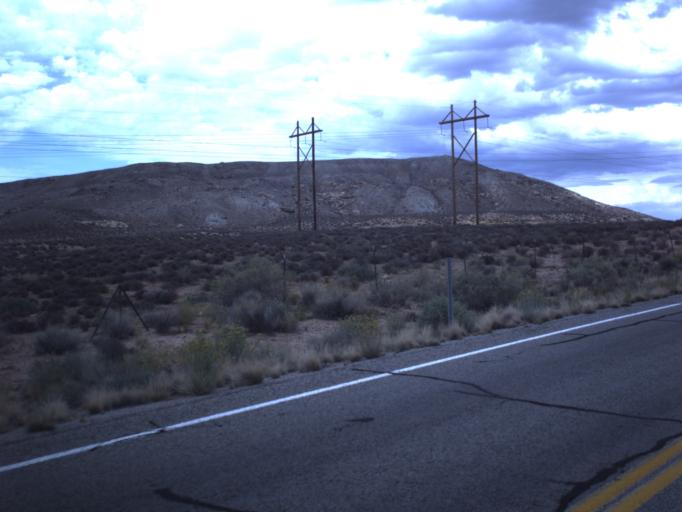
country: US
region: Utah
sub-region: San Juan County
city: Blanding
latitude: 37.2801
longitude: -109.3683
